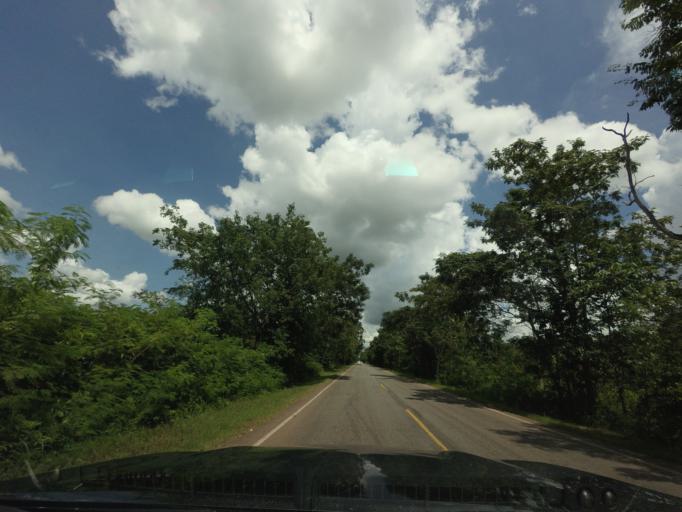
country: TH
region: Changwat Udon Thani
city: Phibun Rak
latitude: 17.5954
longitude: 103.0584
